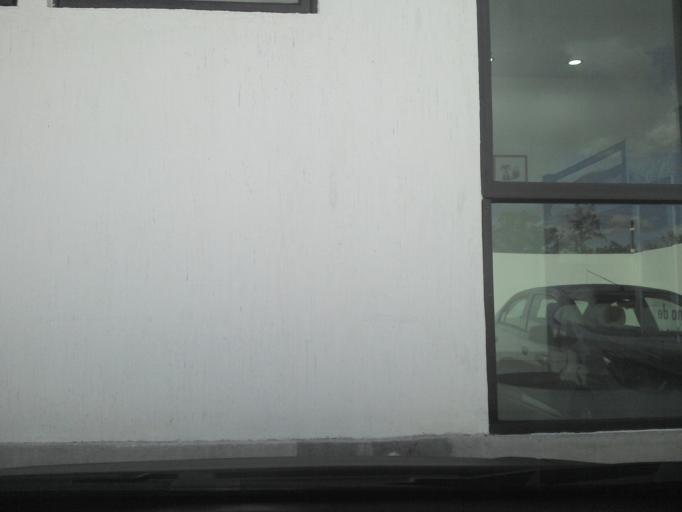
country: MX
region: Jalisco
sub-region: Tlajomulco de Zuniga
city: Palomar
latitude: 20.6191
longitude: -103.4507
